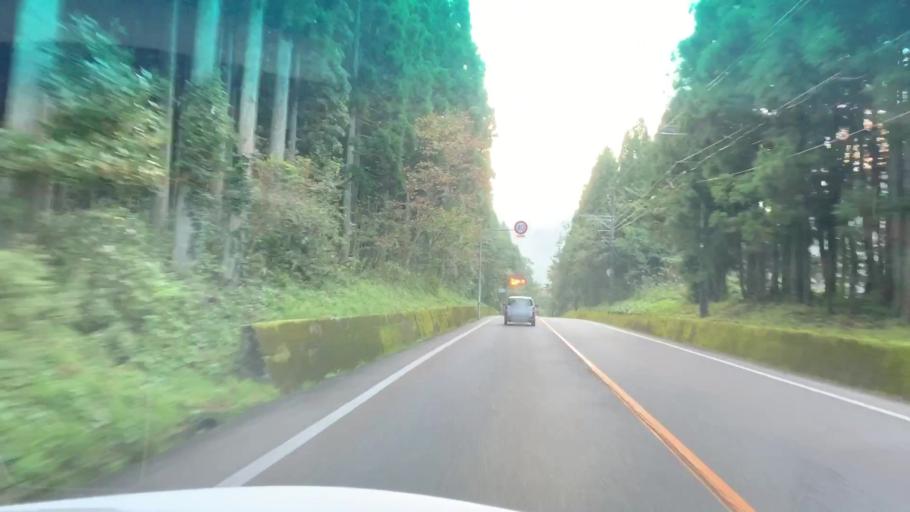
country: JP
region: Toyama
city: Kamiichi
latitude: 36.5769
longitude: 137.3426
